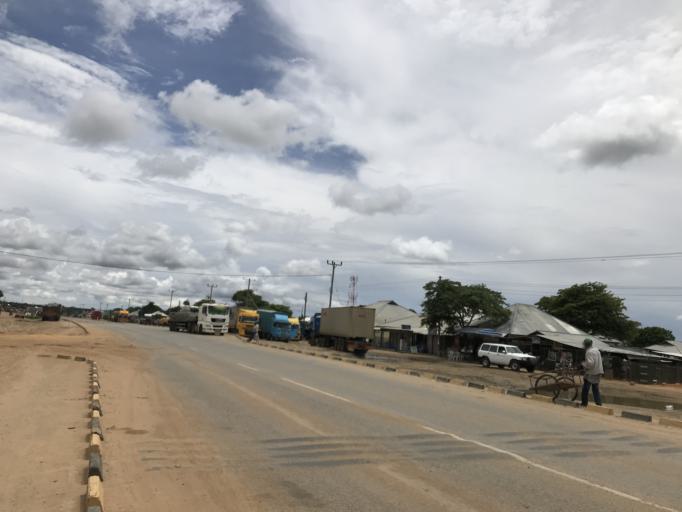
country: TZ
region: Singida
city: Kilimatinde
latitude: -5.7559
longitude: 34.8257
